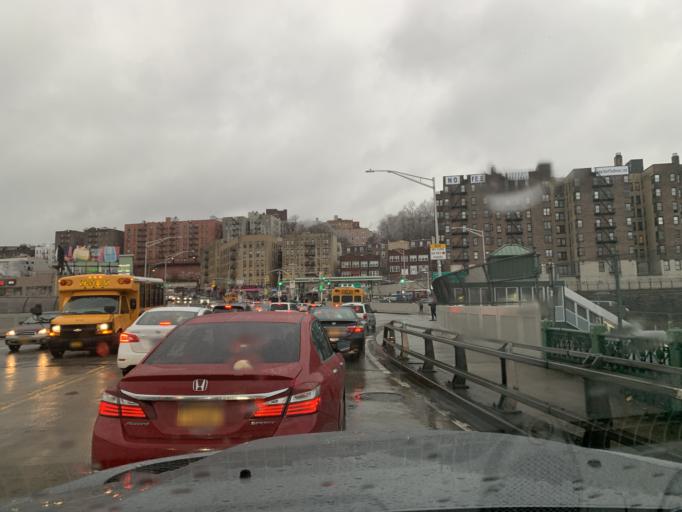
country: US
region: New York
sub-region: New York County
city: Inwood
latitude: 40.8622
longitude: -73.9137
